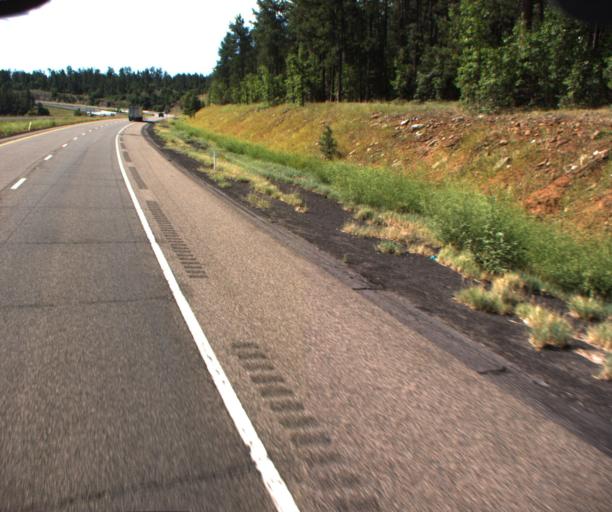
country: US
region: Arizona
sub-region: Coconino County
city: Sedona
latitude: 34.8694
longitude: -111.6299
